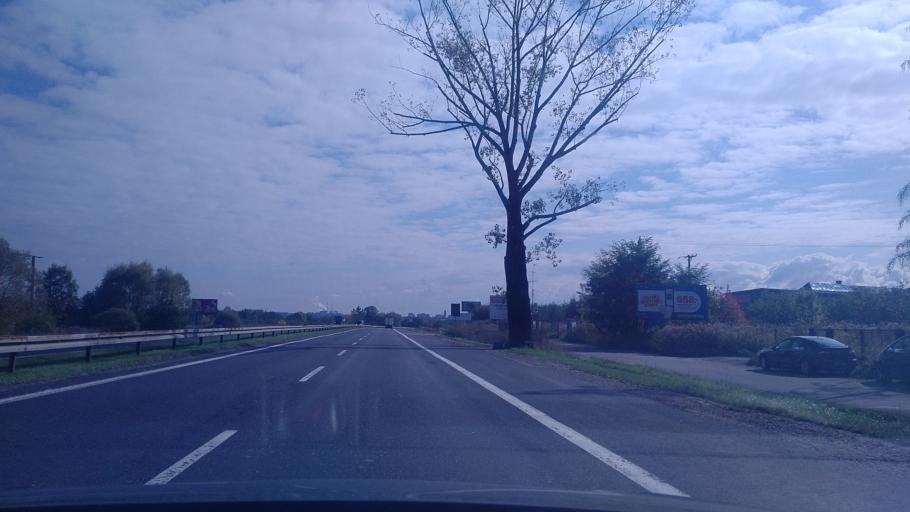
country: PL
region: Lesser Poland Voivodeship
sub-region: Powiat krakowski
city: Modlniczka
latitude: 50.1051
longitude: 19.8836
